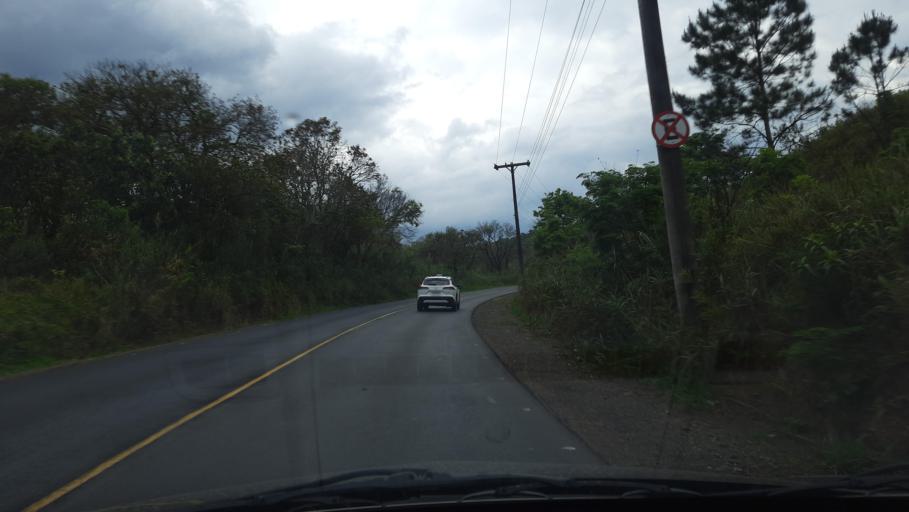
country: BR
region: Sao Paulo
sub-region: Caieiras
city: Caieiras
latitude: -23.3648
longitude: -46.6689
